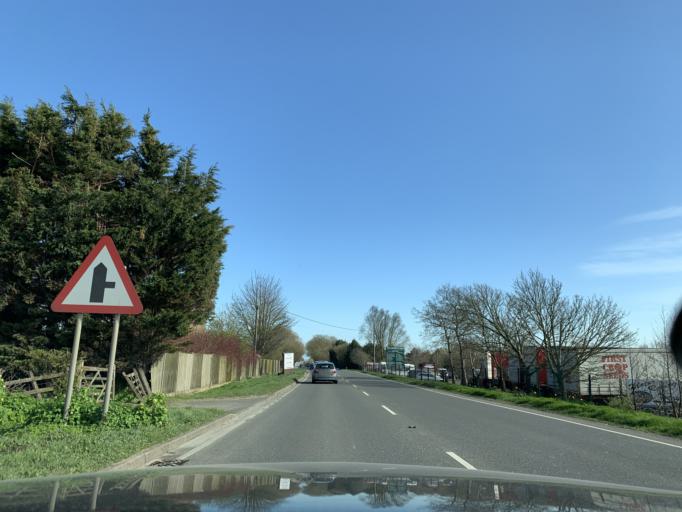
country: GB
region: England
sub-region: Kent
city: Romney Marsh
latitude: 50.9925
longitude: 0.8881
